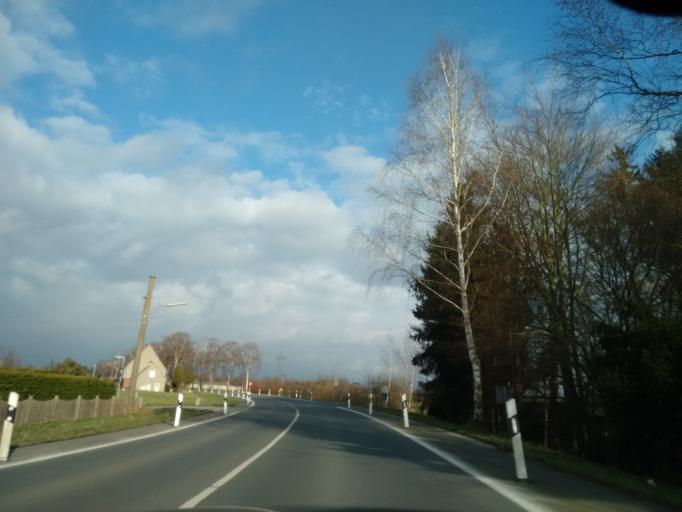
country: DE
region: North Rhine-Westphalia
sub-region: Regierungsbezirk Arnsberg
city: Lippstadt
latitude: 51.6869
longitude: 8.4099
